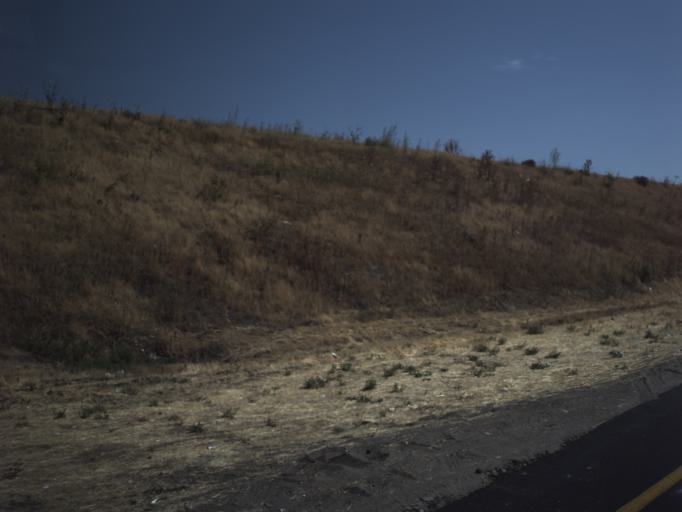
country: US
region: Utah
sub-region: Weber County
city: Roy
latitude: 41.1615
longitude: -112.0238
